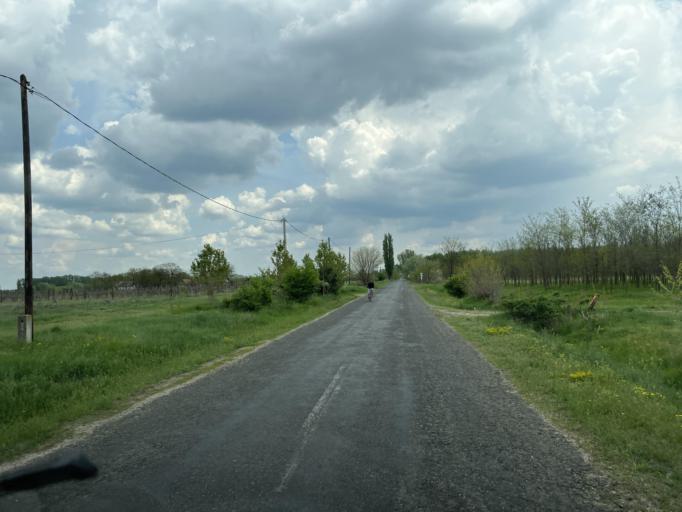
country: HU
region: Pest
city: Nagykoros
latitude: 47.0907
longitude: 19.7674
